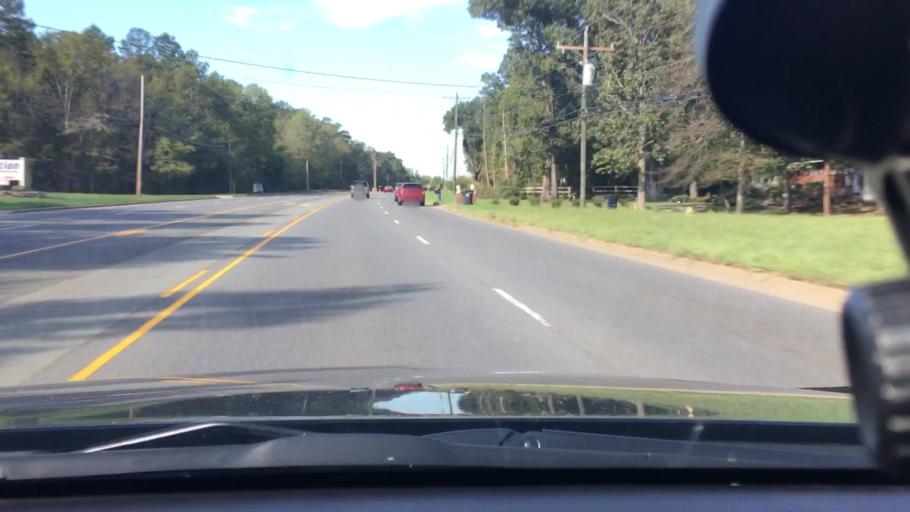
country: US
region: North Carolina
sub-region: Cabarrus County
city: Midland
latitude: 35.2504
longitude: -80.5087
